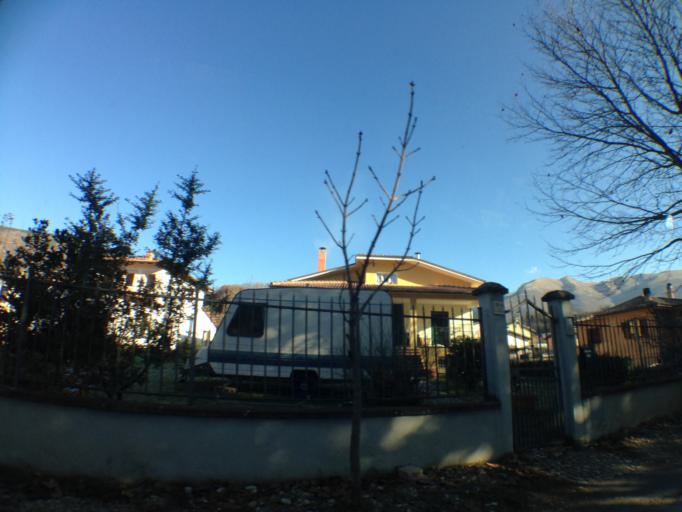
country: IT
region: Umbria
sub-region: Provincia di Perugia
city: Norcia
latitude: 42.7976
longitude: 13.0967
